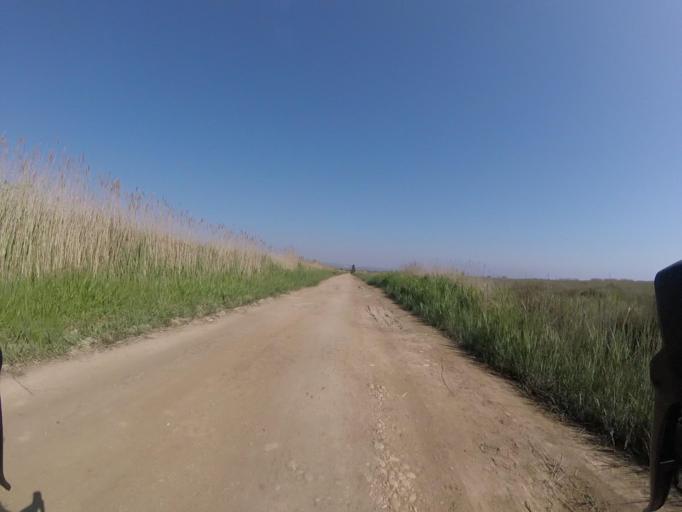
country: ES
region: Valencia
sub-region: Provincia de Castello
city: Orpesa/Oropesa del Mar
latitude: 40.1402
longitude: 0.1640
